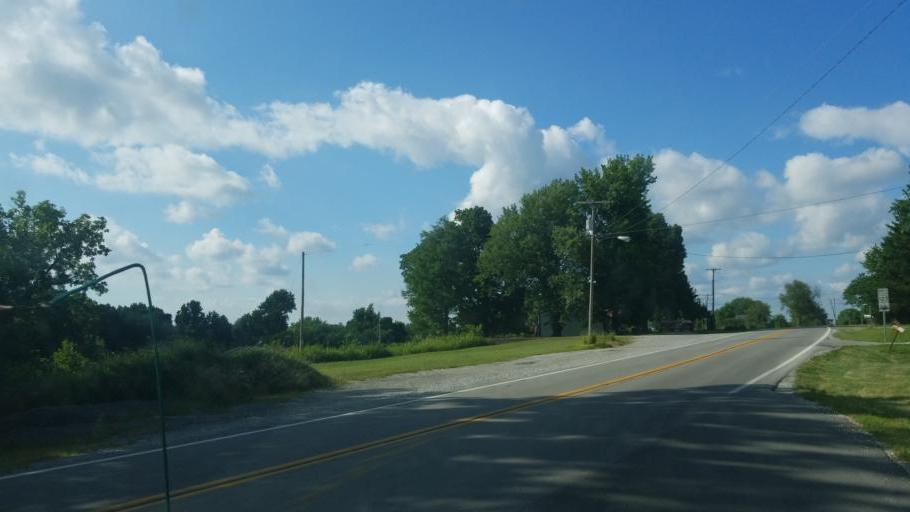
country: US
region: Illinois
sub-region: Union County
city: Cobden
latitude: 37.5764
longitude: -89.3208
